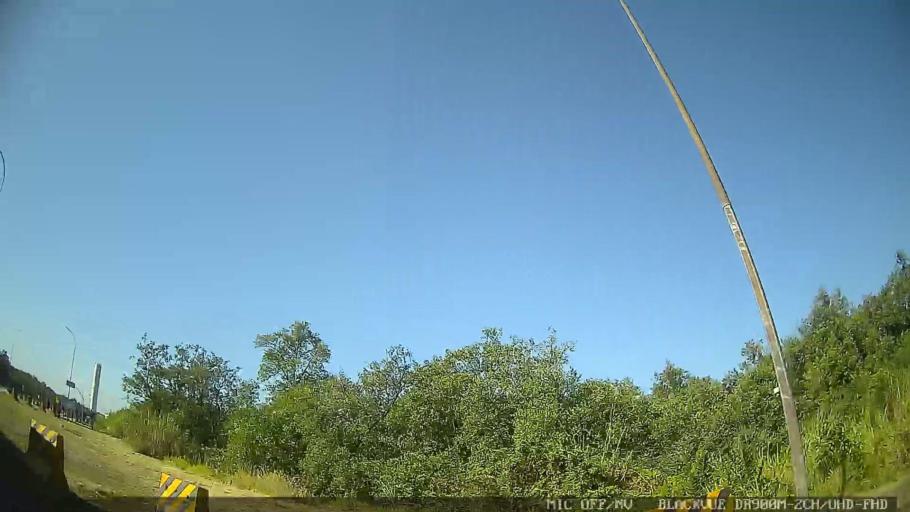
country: BR
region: Sao Paulo
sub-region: Santos
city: Santos
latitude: -23.9087
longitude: -46.3137
